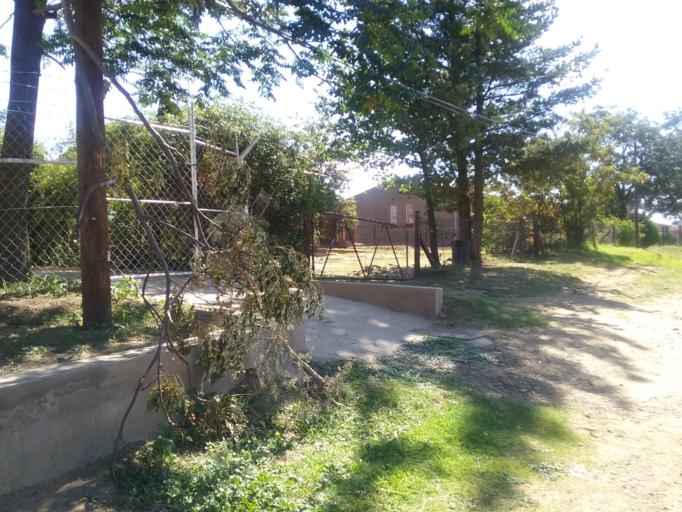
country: LS
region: Maseru
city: Maseru
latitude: -29.3022
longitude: 27.4669
